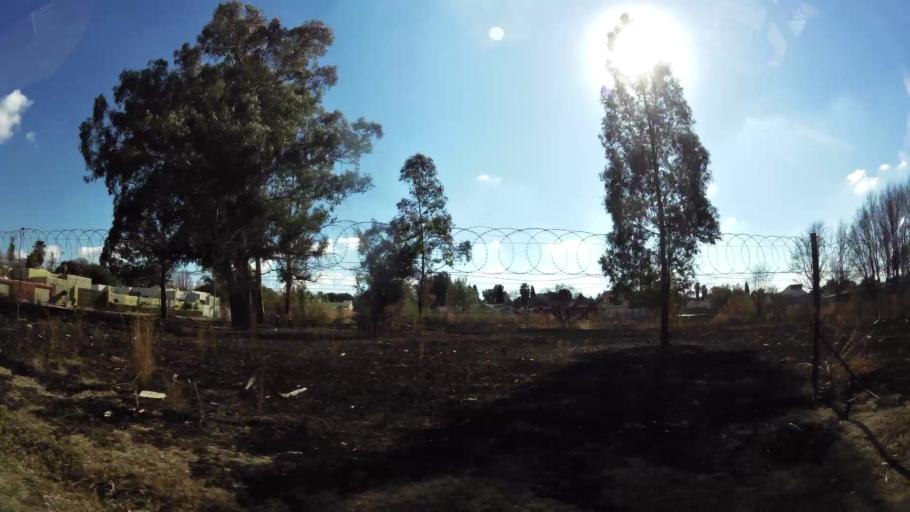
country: ZA
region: Gauteng
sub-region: City of Johannesburg Metropolitan Municipality
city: Roodepoort
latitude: -26.1505
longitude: 27.8353
